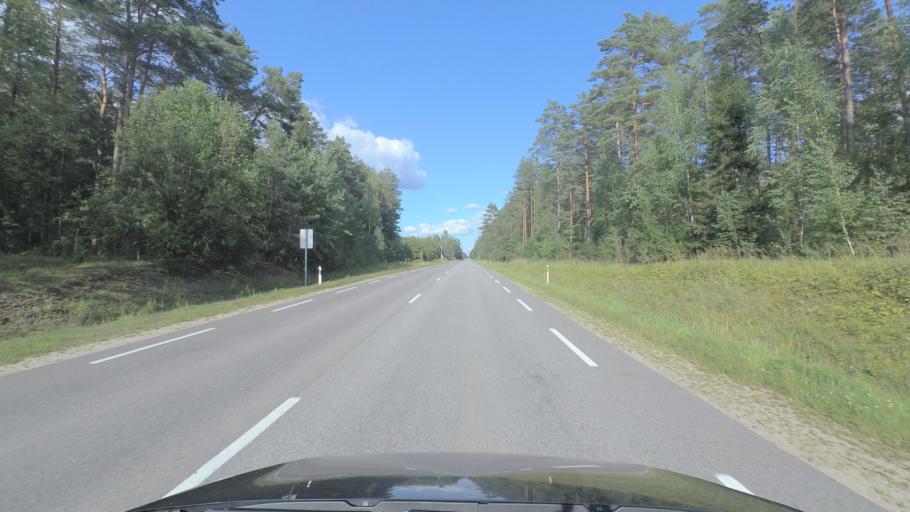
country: LT
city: Pabrade
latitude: 54.9560
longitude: 25.6797
